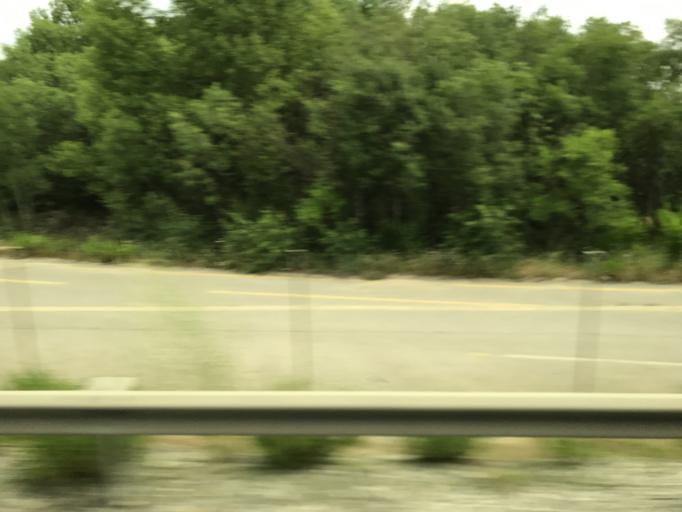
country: ES
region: Madrid
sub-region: Provincia de Madrid
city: La Cabrera
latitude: 40.8980
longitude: -3.6053
